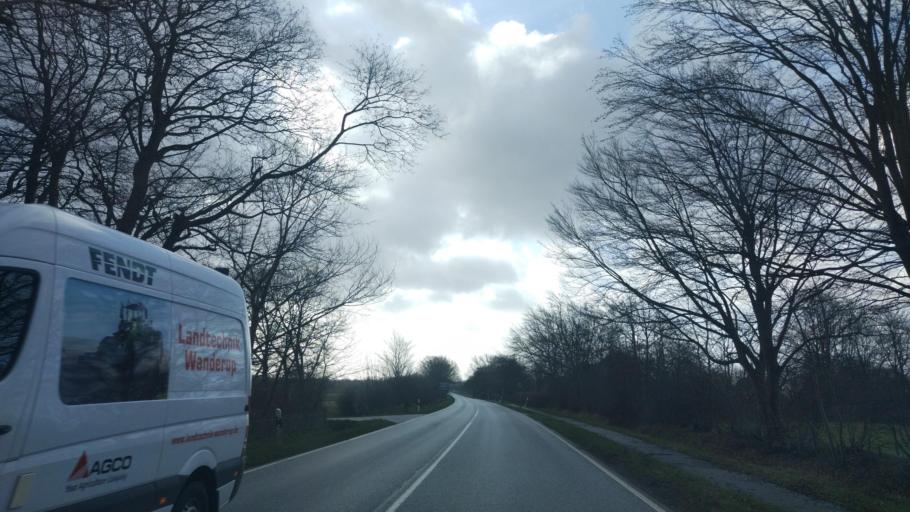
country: DE
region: Schleswig-Holstein
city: Janneby
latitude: 54.6606
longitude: 9.2944
